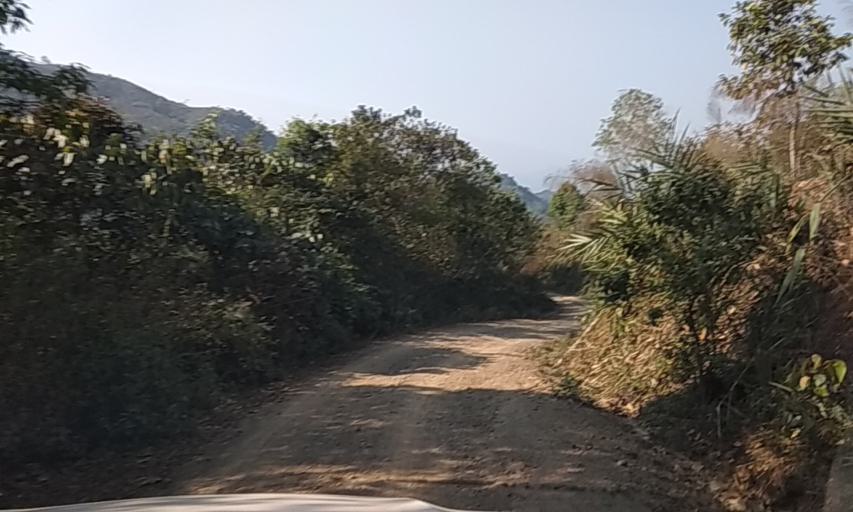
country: LA
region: Phongsali
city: Phongsali
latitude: 21.6936
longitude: 102.0906
